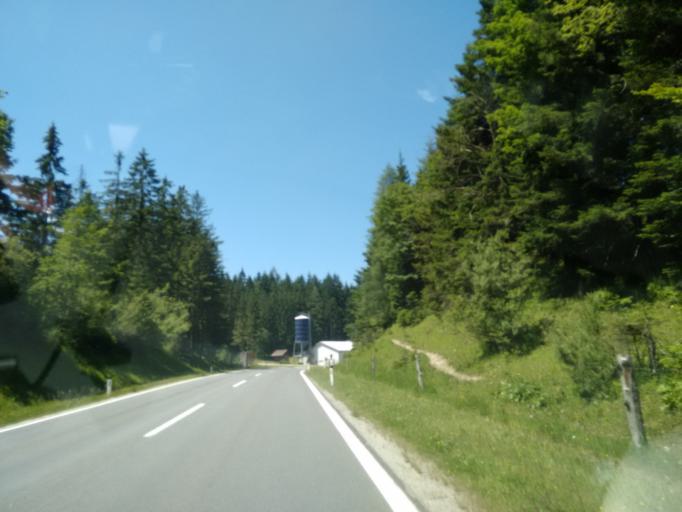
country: AT
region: Styria
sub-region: Politischer Bezirk Liezen
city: Altaussee
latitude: 47.6221
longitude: 13.6957
